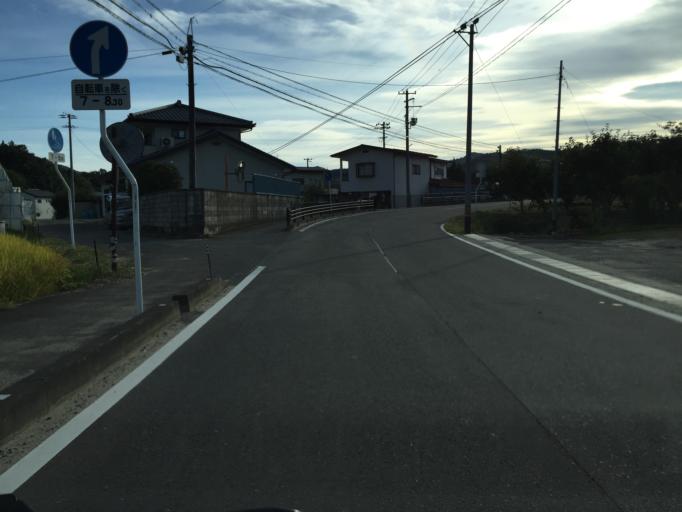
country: JP
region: Fukushima
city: Hobaramachi
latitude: 37.7905
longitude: 140.5981
